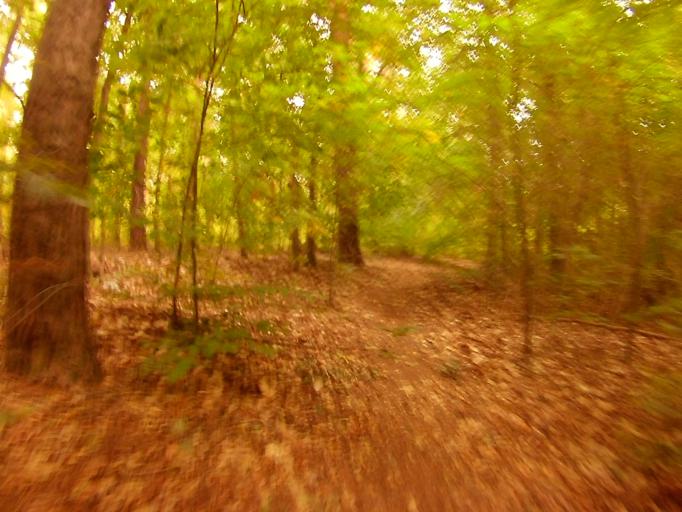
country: DE
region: Brandenburg
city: Zeuthen
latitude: 52.4015
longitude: 13.6177
